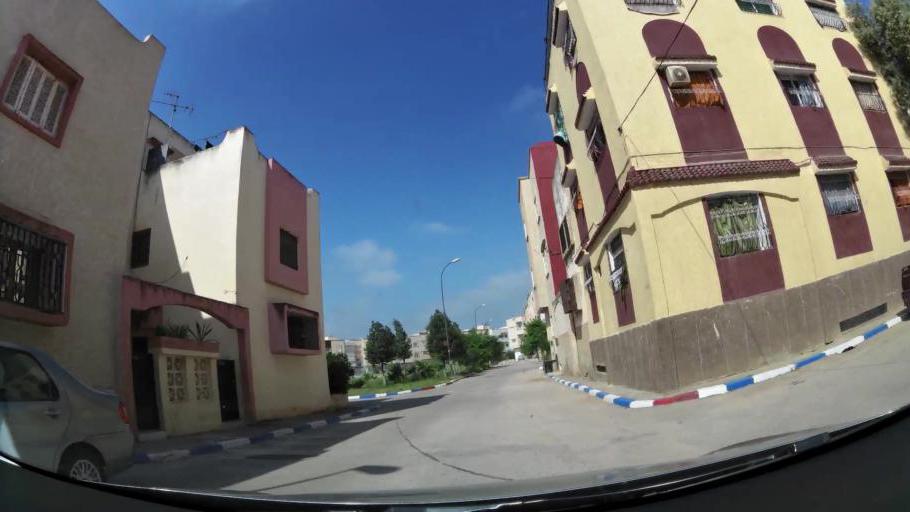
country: MA
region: Fes-Boulemane
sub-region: Fes
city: Fes
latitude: 34.0557
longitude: -5.0225
